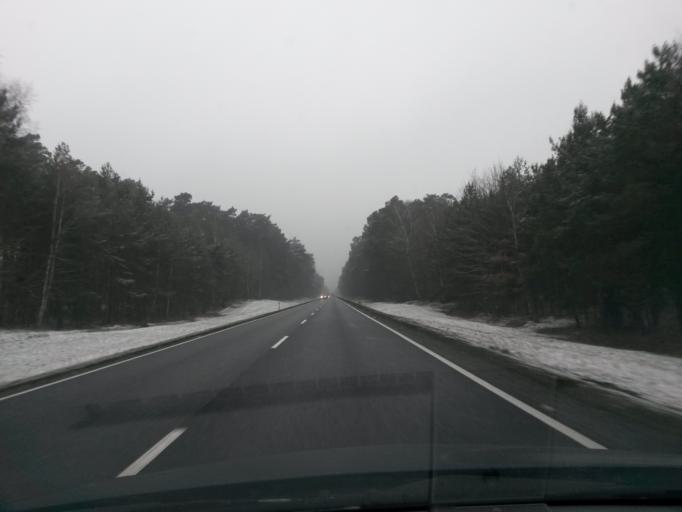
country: PL
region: Kujawsko-Pomorskie
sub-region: Powiat torunski
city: Wielka Nieszawka
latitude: 53.0058
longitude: 18.4449
